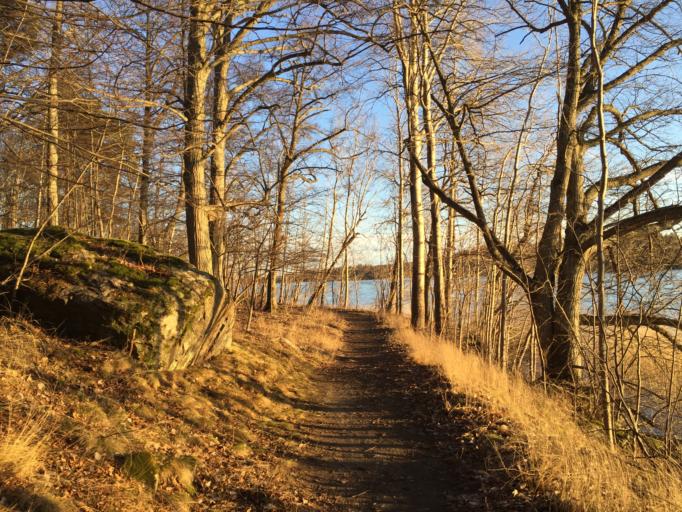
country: SE
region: Stockholm
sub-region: Salems Kommun
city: Ronninge
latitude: 59.2596
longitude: 17.7102
